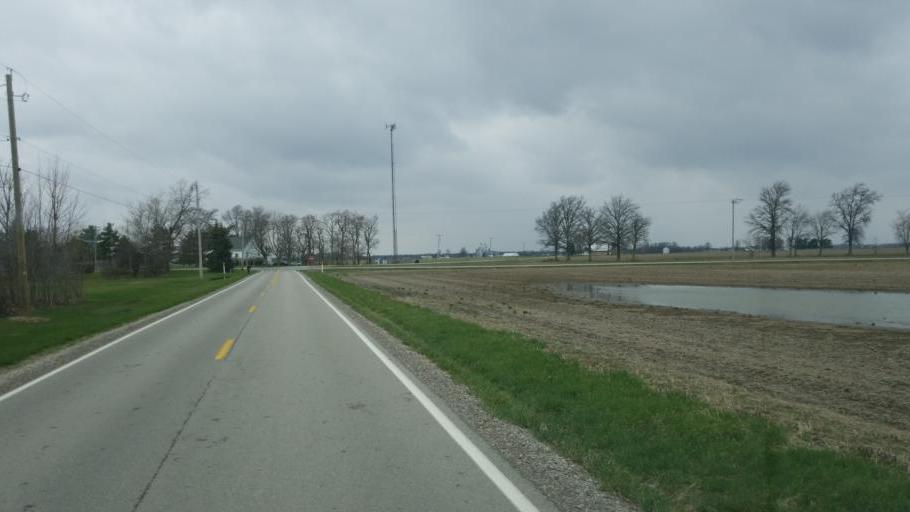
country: US
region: Ohio
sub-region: Union County
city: Richwood
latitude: 40.4191
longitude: -83.2470
